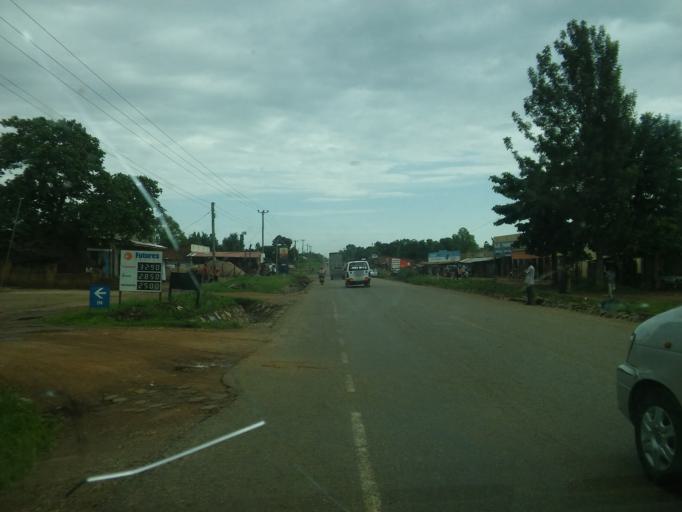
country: UG
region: Eastern Region
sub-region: Mbale District
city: Mbale
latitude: 1.1118
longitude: 34.1716
